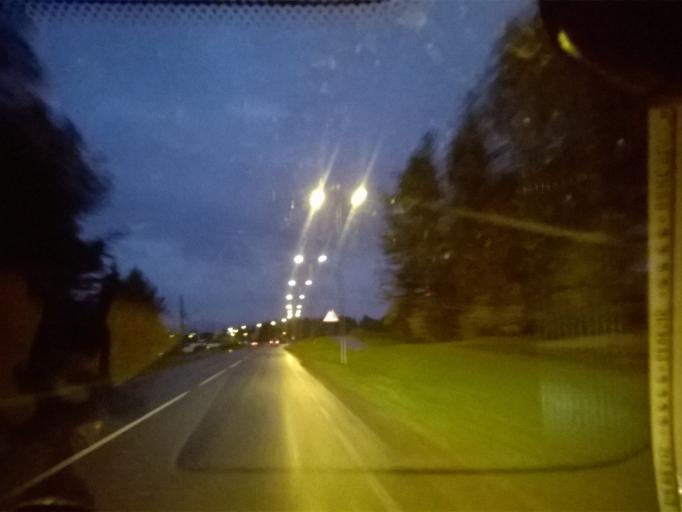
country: EE
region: Harju
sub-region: Viimsi vald
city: Viimsi
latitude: 59.4961
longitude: 24.8744
